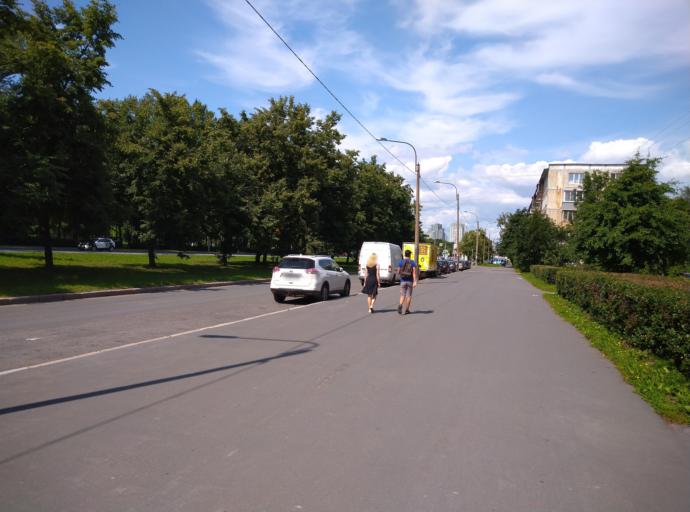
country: RU
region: St.-Petersburg
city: Kupchino
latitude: 59.8625
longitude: 30.3378
